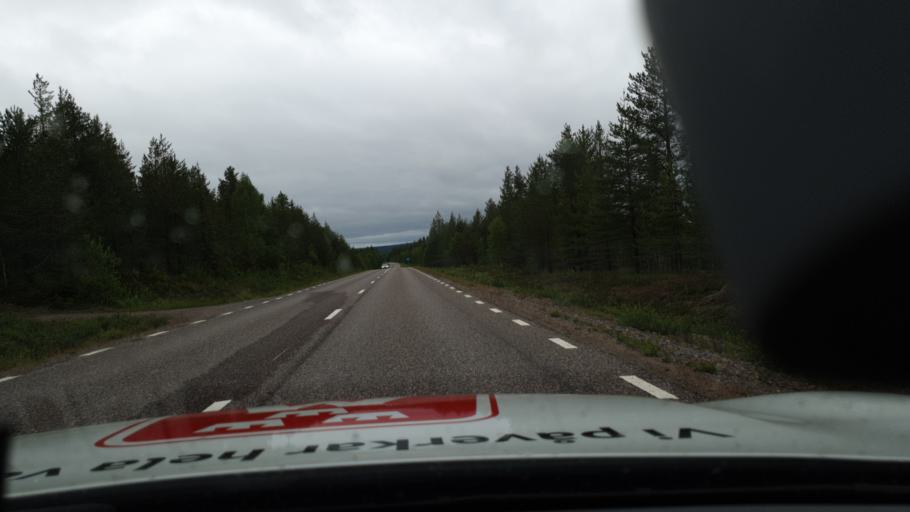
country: SE
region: Norrbotten
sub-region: Pajala Kommun
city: Pajala
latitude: 67.1776
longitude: 23.5005
